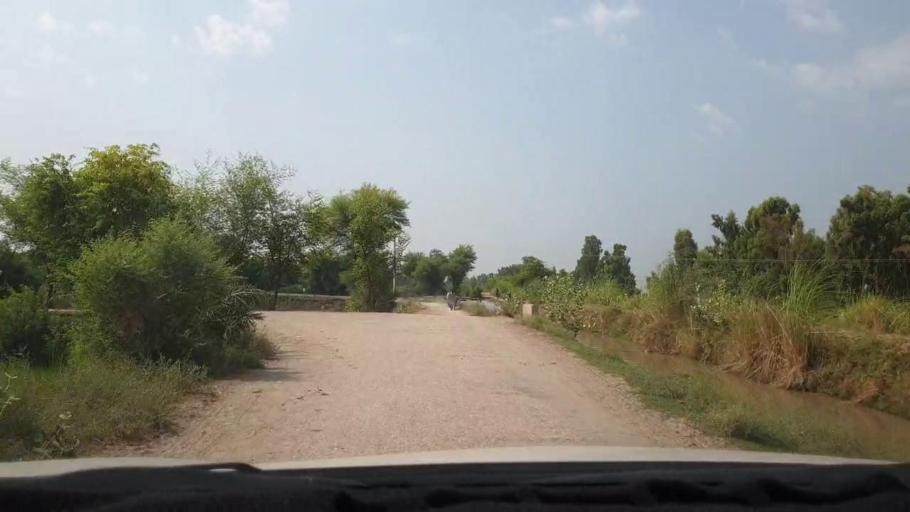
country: PK
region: Sindh
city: Dokri
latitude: 27.3908
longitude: 68.1189
